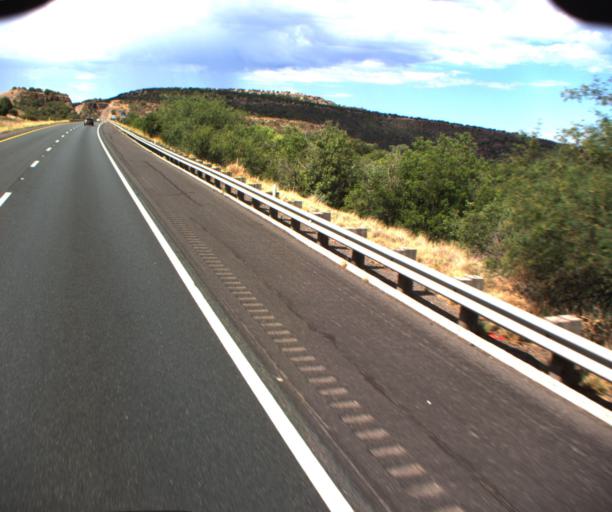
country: US
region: Arizona
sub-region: Yavapai County
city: Camp Verde
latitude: 34.5069
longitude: -111.9980
